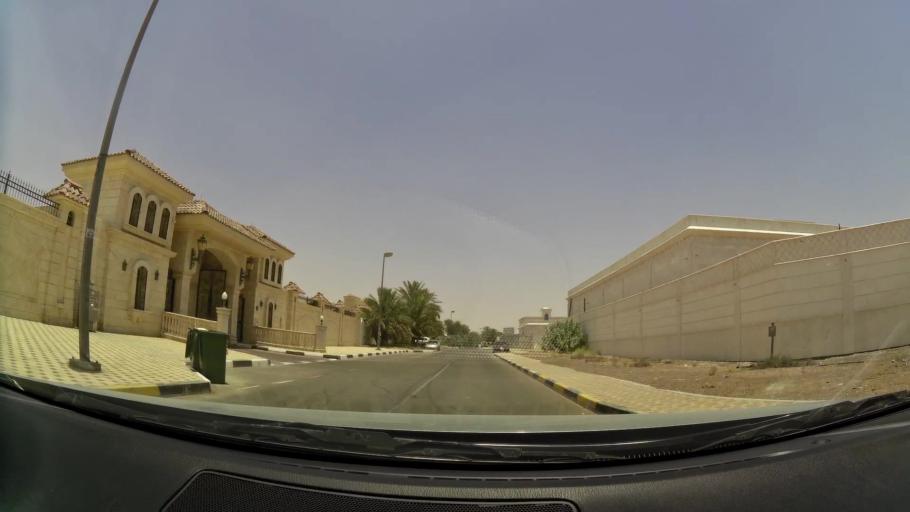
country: OM
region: Al Buraimi
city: Al Buraymi
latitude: 24.2710
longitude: 55.7274
